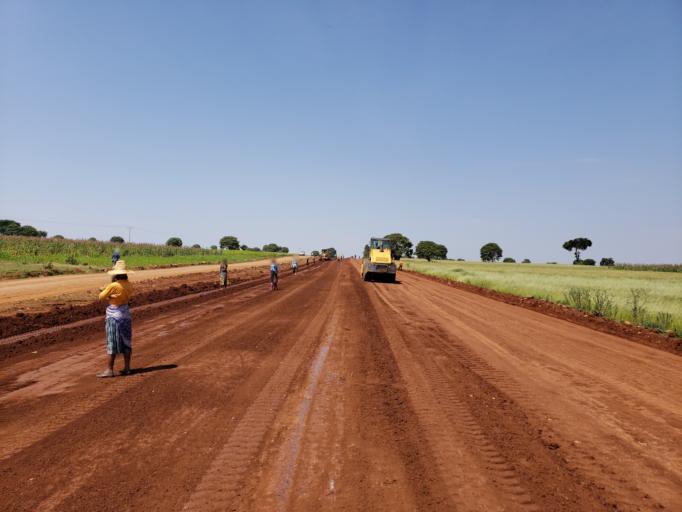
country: ET
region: Amhara
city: Debre Mark'os
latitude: 10.3196
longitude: 37.4121
